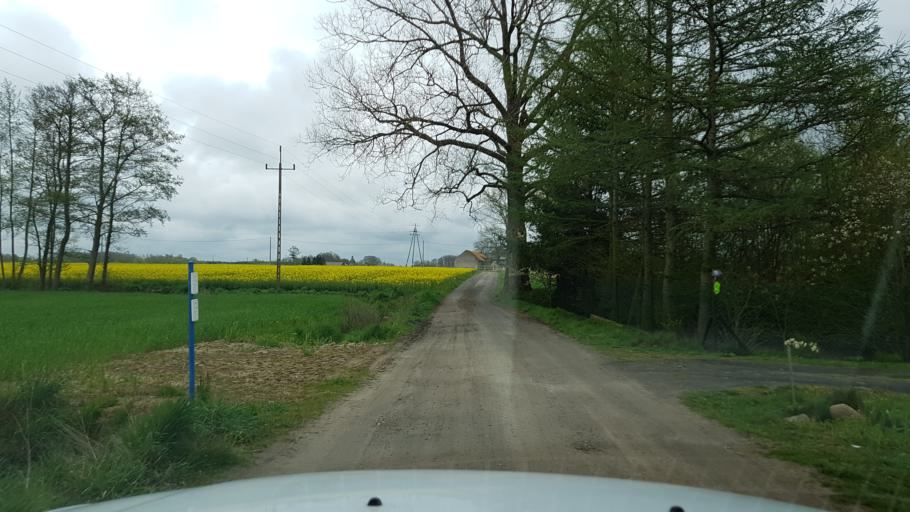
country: PL
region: West Pomeranian Voivodeship
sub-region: Powiat kolobrzeski
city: Ryman
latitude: 54.0340
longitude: 15.4758
